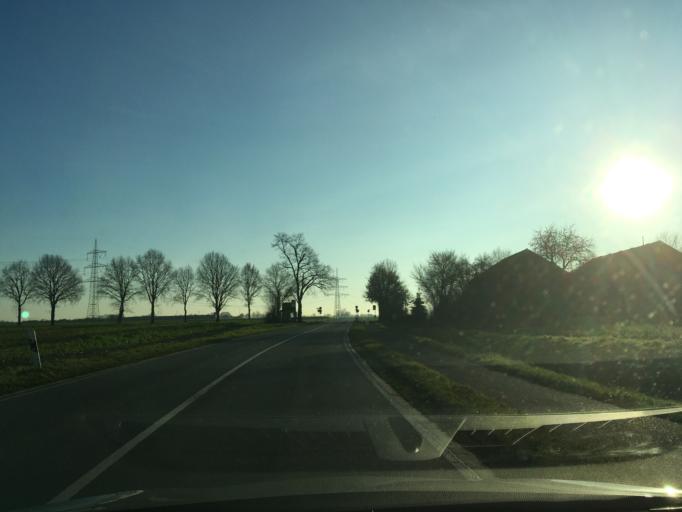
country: DE
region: North Rhine-Westphalia
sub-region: Regierungsbezirk Munster
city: Ahaus
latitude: 52.1045
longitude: 6.9633
